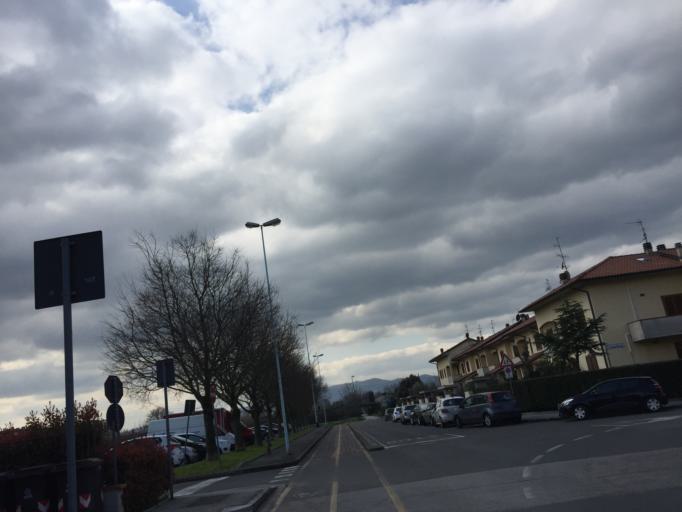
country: IT
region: Tuscany
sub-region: Provincia di Prato
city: Fornacelle
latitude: 43.8961
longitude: 11.0580
